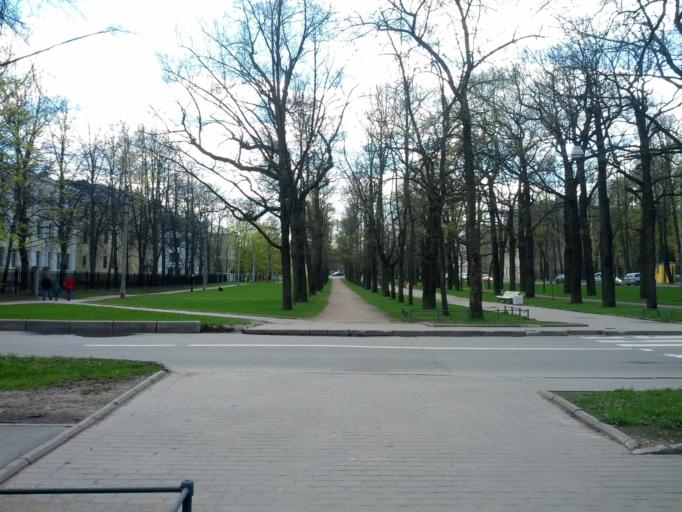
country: RU
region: St.-Petersburg
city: Pushkin
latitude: 59.7179
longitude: 30.4227
